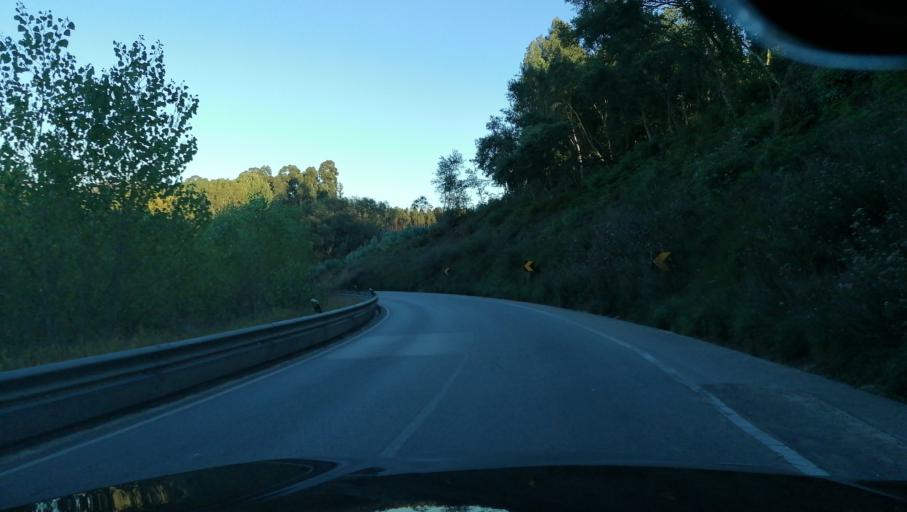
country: PT
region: Aveiro
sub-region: Agueda
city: Agueda
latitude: 40.5578
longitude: -8.4815
